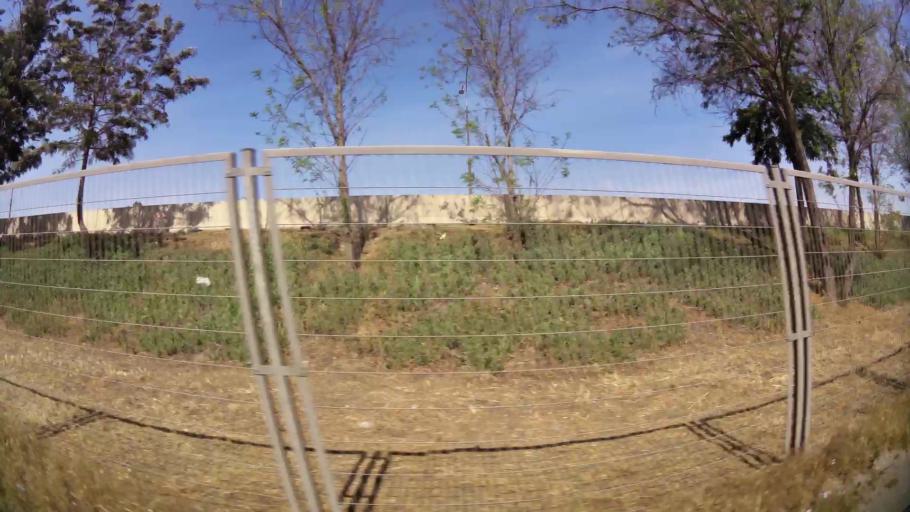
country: CL
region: Santiago Metropolitan
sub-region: Provincia de Maipo
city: San Bernardo
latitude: -33.5496
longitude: -70.7004
